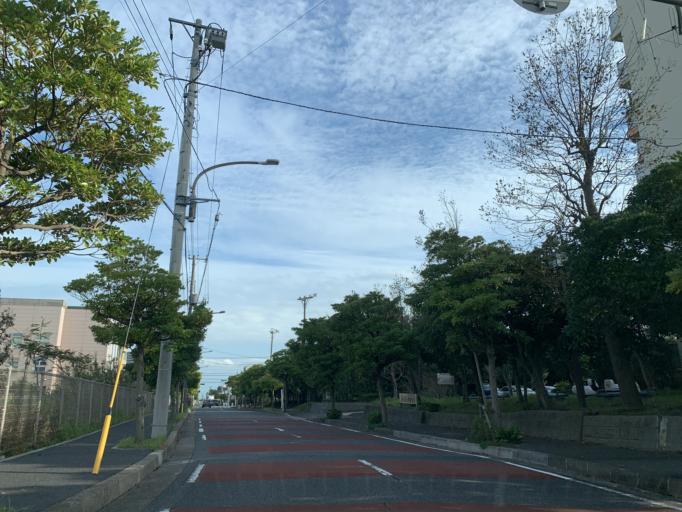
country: JP
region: Tokyo
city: Urayasu
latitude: 35.6377
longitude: 139.9095
